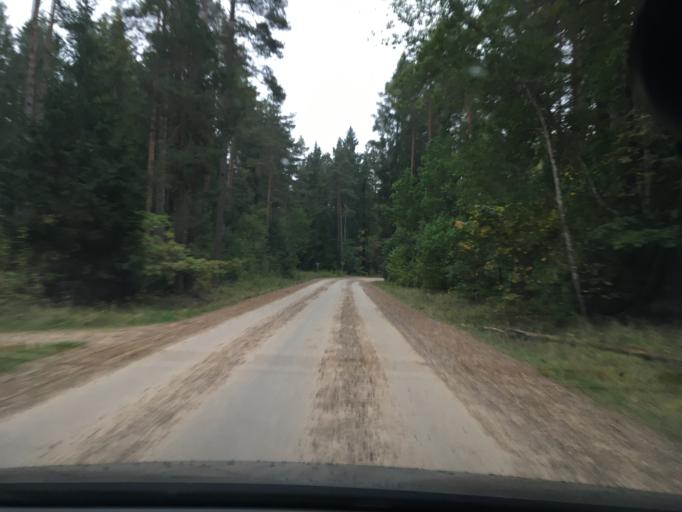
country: LV
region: Kuldigas Rajons
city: Kuldiga
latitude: 56.9864
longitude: 21.9755
